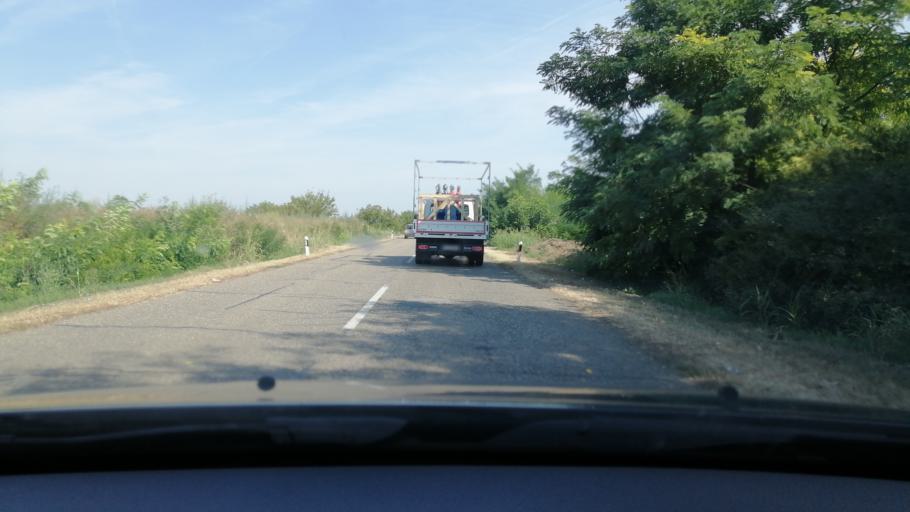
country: RS
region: Autonomna Pokrajina Vojvodina
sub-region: Juznobanatski Okrug
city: Kovacica
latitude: 45.1244
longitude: 20.6164
